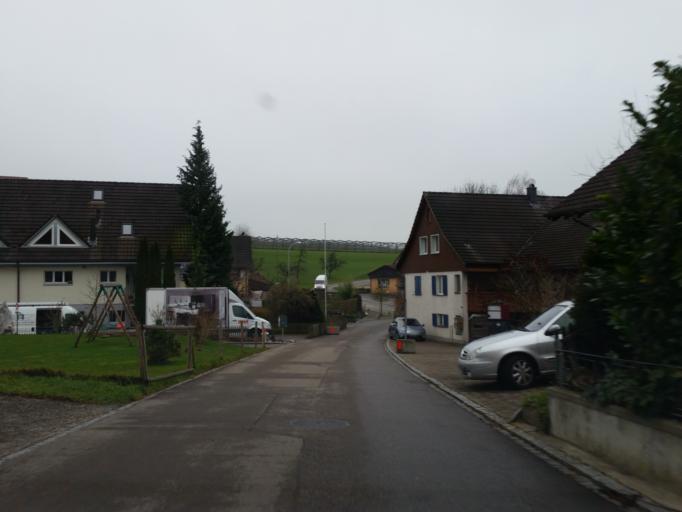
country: CH
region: Thurgau
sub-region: Weinfelden District
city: Erlen
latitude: 47.5396
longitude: 9.2328
